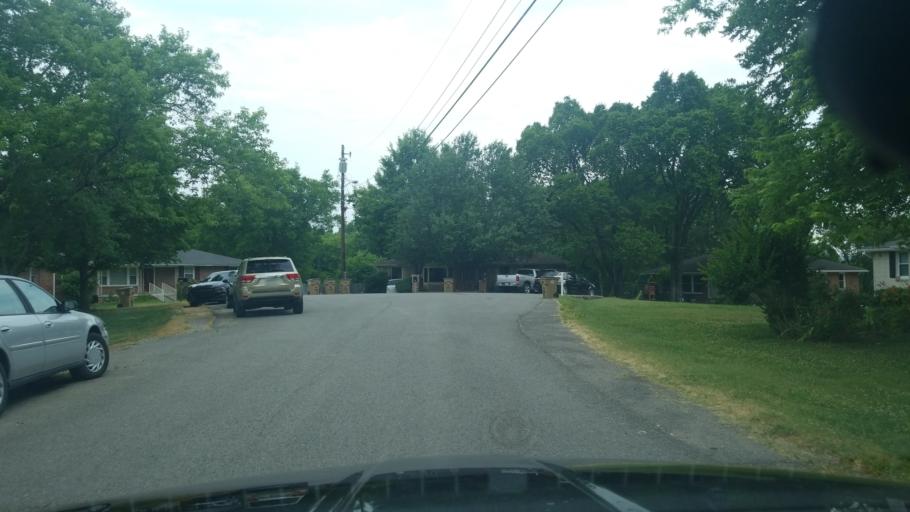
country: US
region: Tennessee
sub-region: Davidson County
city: Goodlettsville
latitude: 36.2623
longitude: -86.7474
